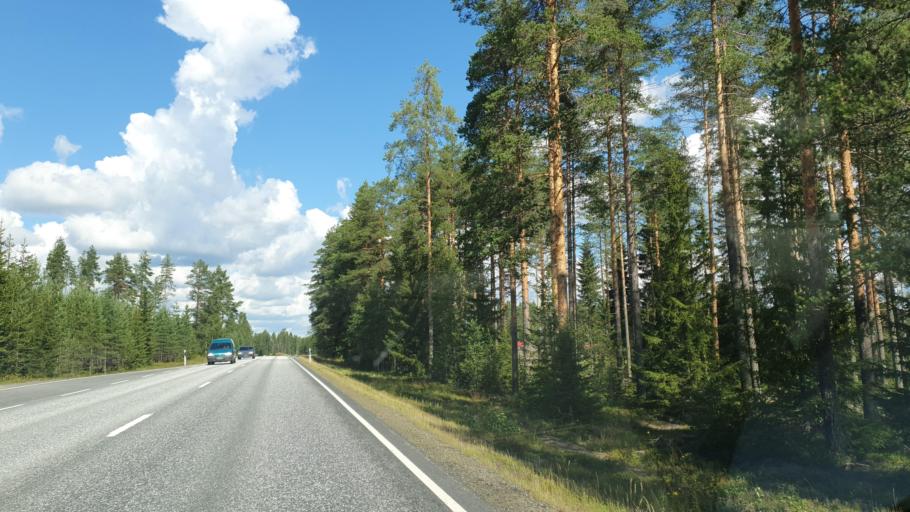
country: FI
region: Northern Savo
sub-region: Ylae-Savo
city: Sonkajaervi
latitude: 63.8278
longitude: 27.4211
